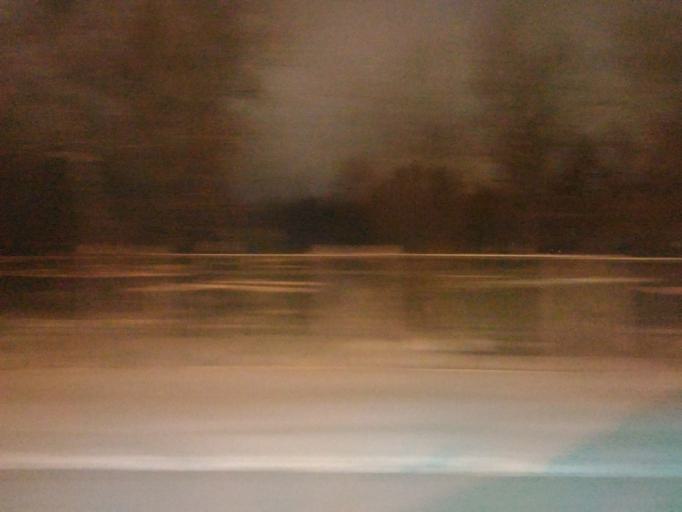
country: RU
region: Ulyanovsk
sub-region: Ulyanovskiy Rayon
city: Ulyanovsk
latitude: 54.3256
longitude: 48.3635
